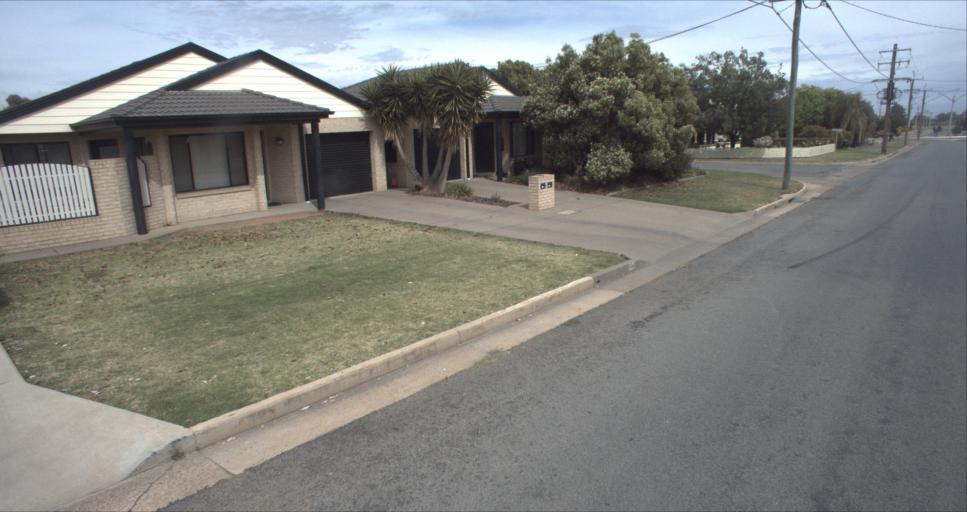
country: AU
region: New South Wales
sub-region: Leeton
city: Leeton
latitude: -34.5482
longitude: 146.4030
